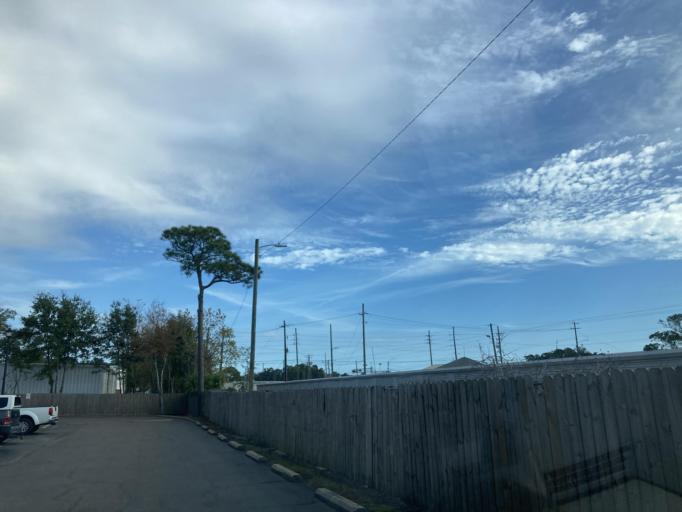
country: US
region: Mississippi
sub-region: Harrison County
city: West Gulfport
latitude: 30.3957
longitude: -88.9944
